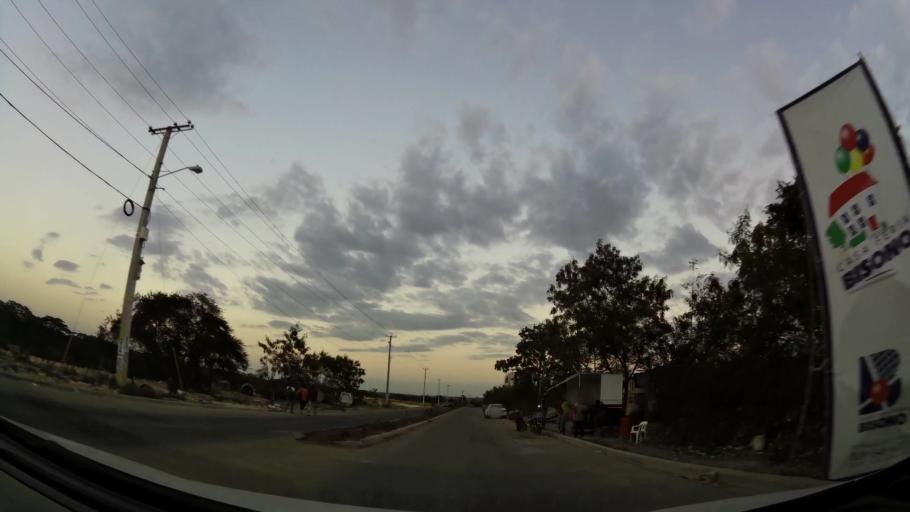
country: DO
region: Nacional
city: La Agustina
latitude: 18.5627
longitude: -69.9406
